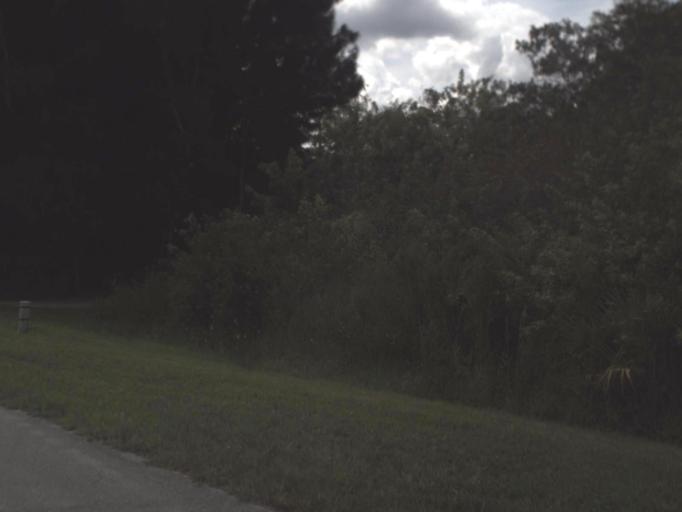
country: US
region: Florida
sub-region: Collier County
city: Lely Resort
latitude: 25.9957
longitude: -81.3472
